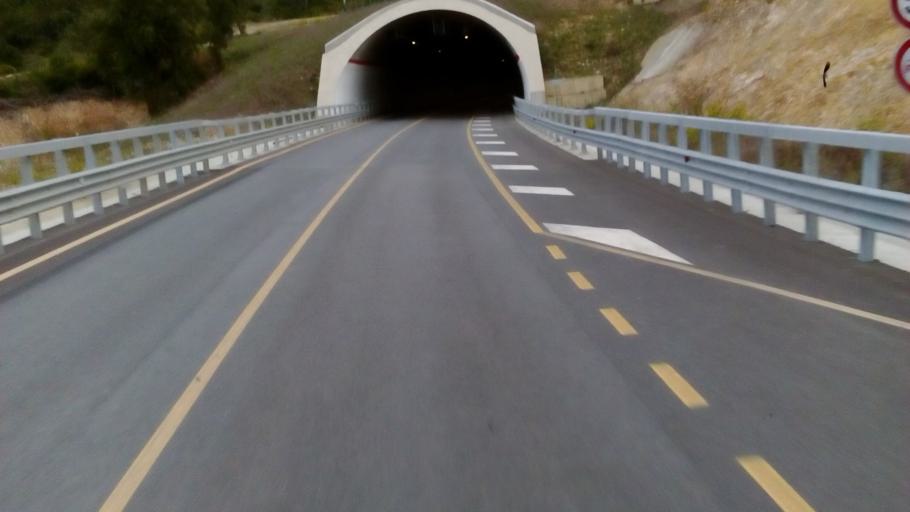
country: IT
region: Tuscany
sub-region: Provincia di Grosseto
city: Civitella Marittima
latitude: 43.0351
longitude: 11.2761
